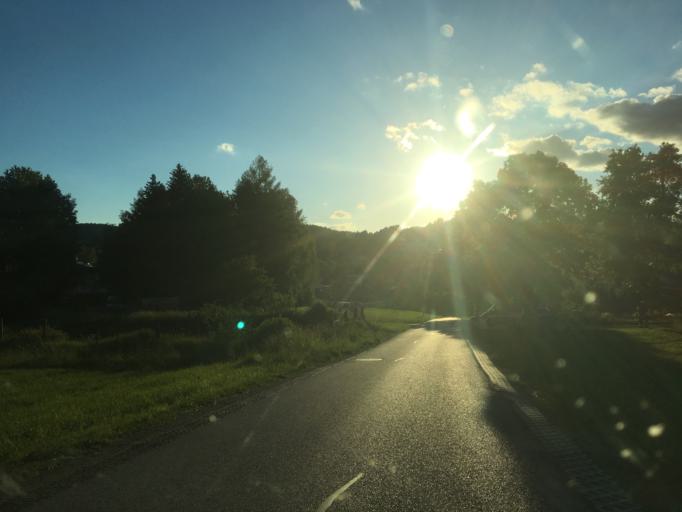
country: AT
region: Upper Austria
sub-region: Politischer Bezirk Urfahr-Umgebung
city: Zwettl an der Rodl
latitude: 48.4647
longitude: 14.2755
